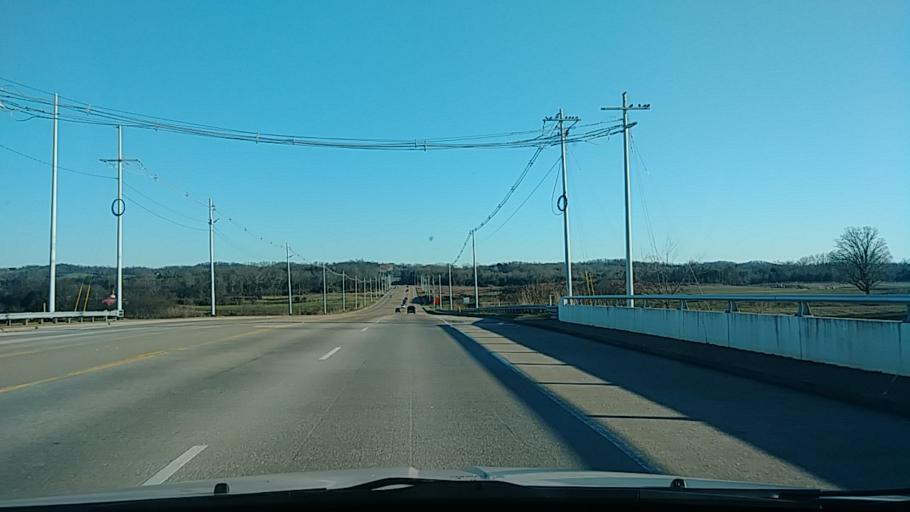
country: US
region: Tennessee
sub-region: Hamblen County
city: Morristown
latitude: 36.1882
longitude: -83.3579
